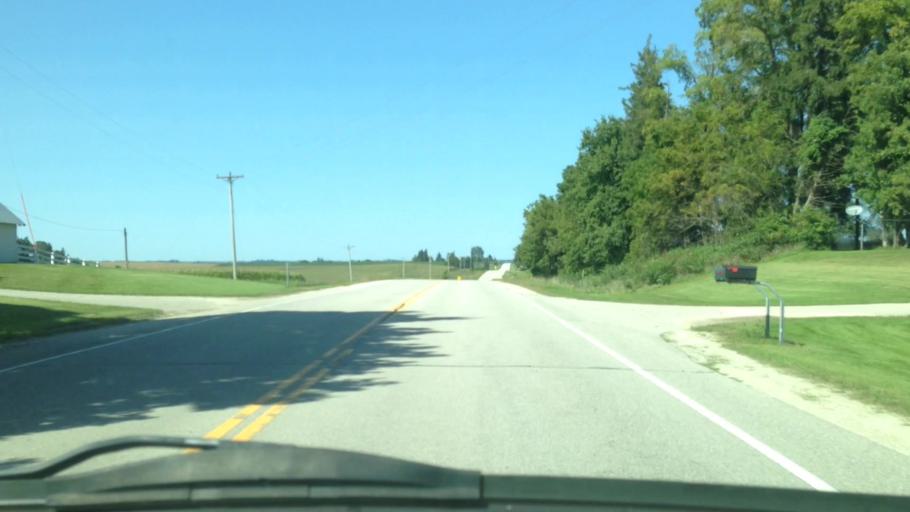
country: US
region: Minnesota
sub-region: Houston County
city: Spring Grove
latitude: 43.6077
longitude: -91.7903
